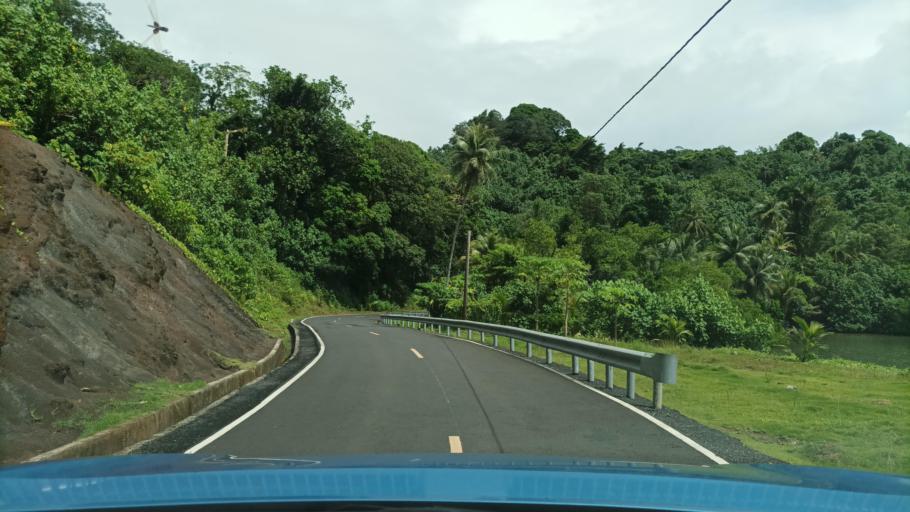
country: FM
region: Pohnpei
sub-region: Madolenihm Municipality
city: Madolenihm Municipality Government
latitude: 6.8622
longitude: 158.3243
